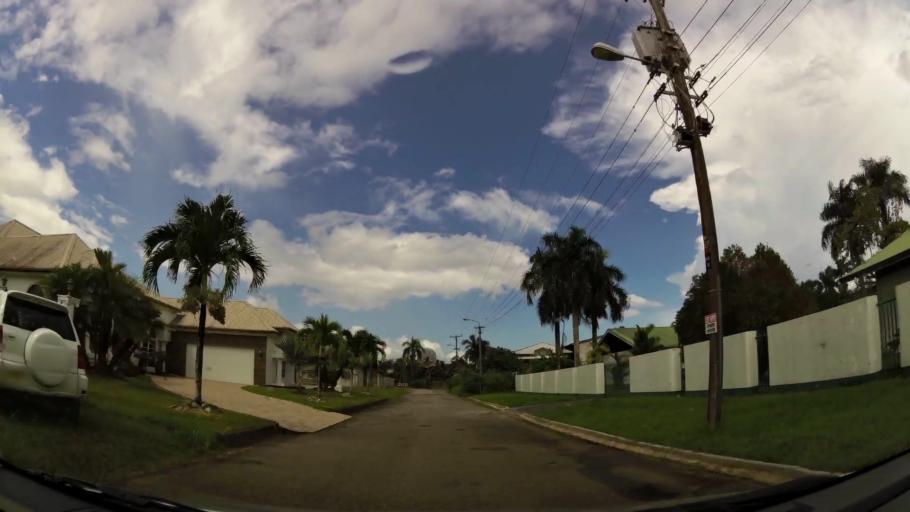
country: SR
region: Paramaribo
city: Paramaribo
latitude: 5.8372
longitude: -55.1258
